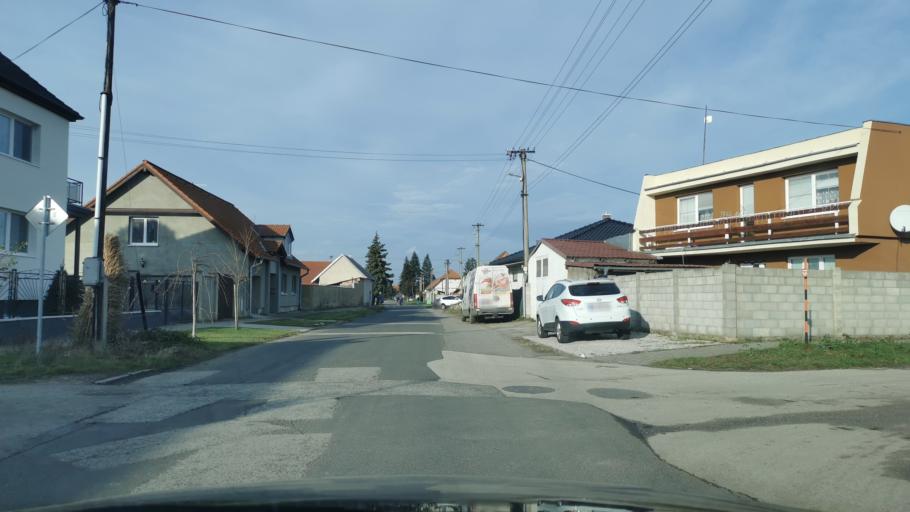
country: SK
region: Trnavsky
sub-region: Okres Skalica
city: Holic
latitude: 48.7841
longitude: 17.1110
